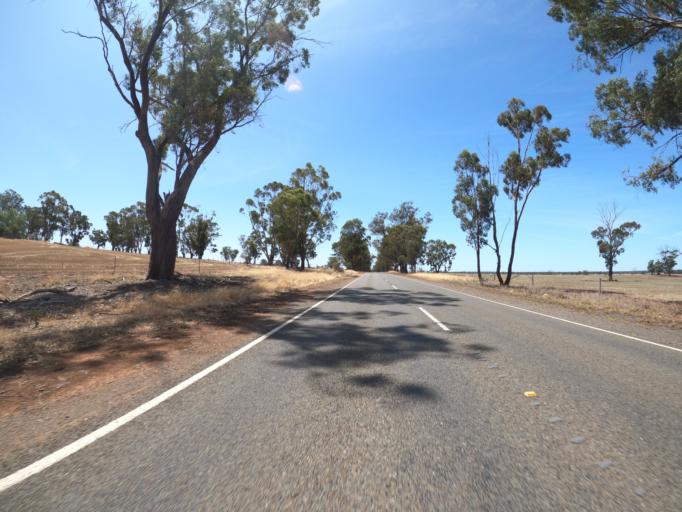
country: AU
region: Victoria
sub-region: Moira
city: Yarrawonga
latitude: -36.1048
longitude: 145.9894
